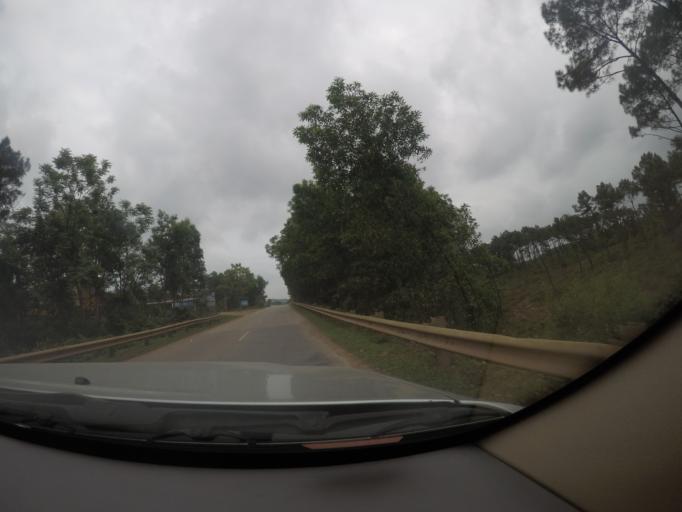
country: VN
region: Quang Binh
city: Kien Giang
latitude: 17.1479
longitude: 106.7568
